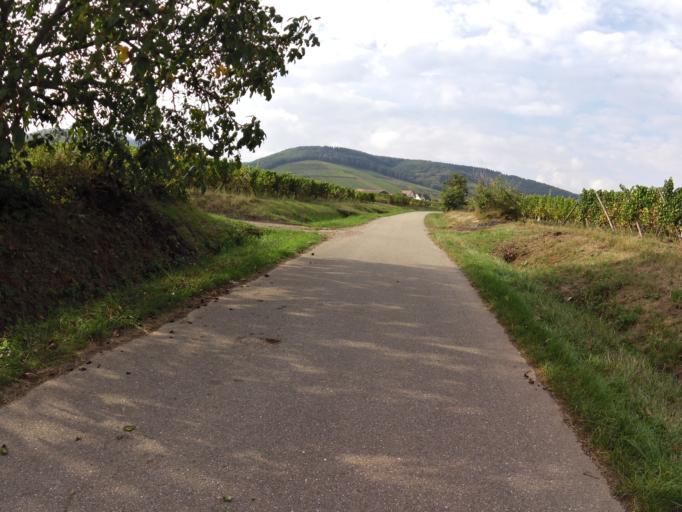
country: FR
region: Alsace
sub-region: Departement du Bas-Rhin
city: Kintzheim
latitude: 48.2368
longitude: 7.3894
